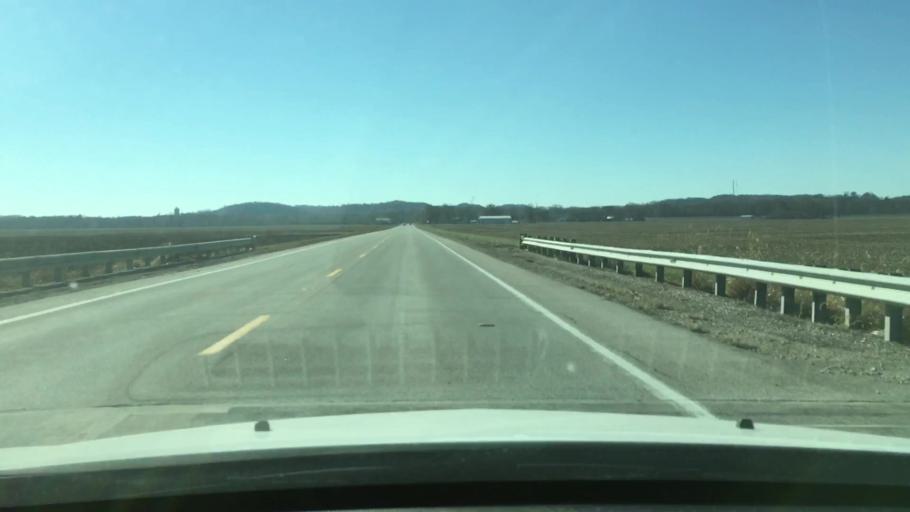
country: US
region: Missouri
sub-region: Pike County
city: Louisiana
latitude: 39.4723
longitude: -91.0236
